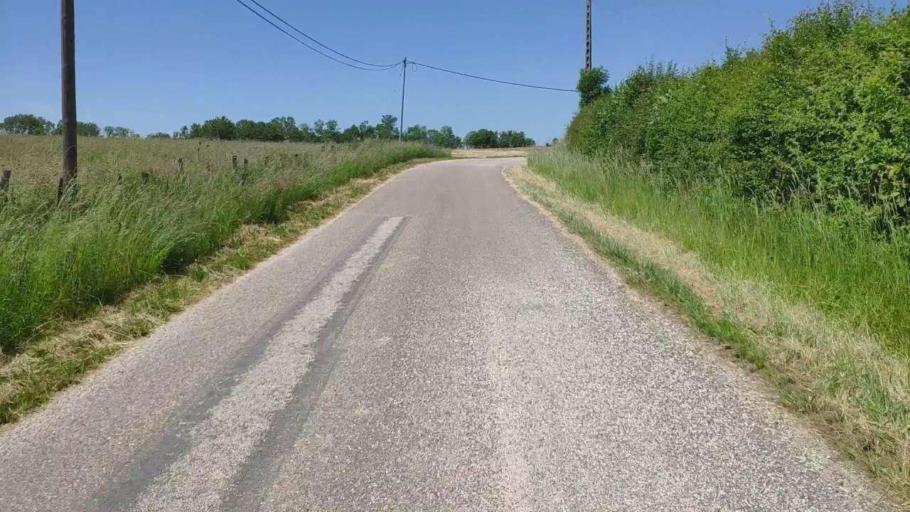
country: FR
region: Franche-Comte
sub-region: Departement du Jura
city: Bletterans
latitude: 46.7535
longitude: 5.4240
